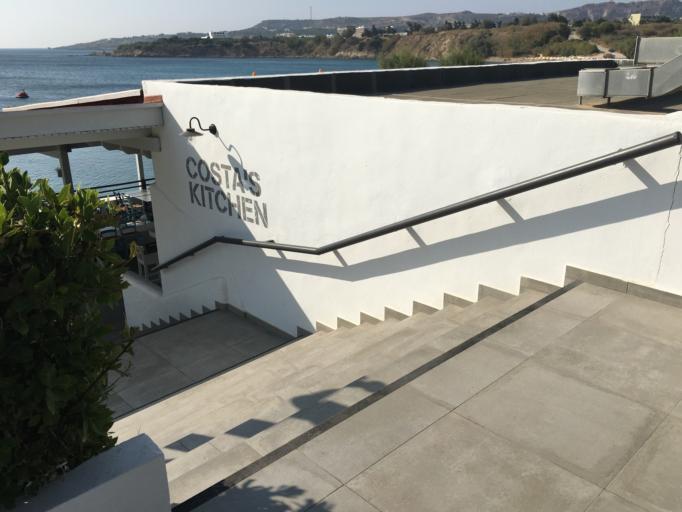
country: GR
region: South Aegean
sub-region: Nomos Dodekanisou
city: Rodos
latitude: 36.4062
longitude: 28.2286
